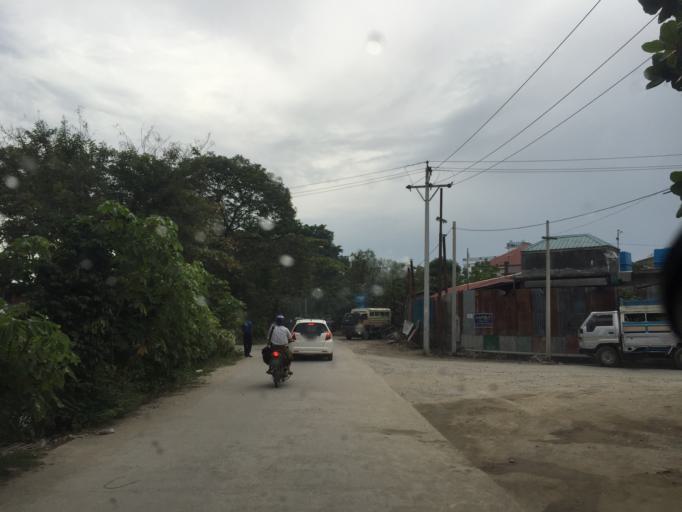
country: MM
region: Mandalay
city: Mandalay
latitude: 21.9718
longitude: 96.1090
